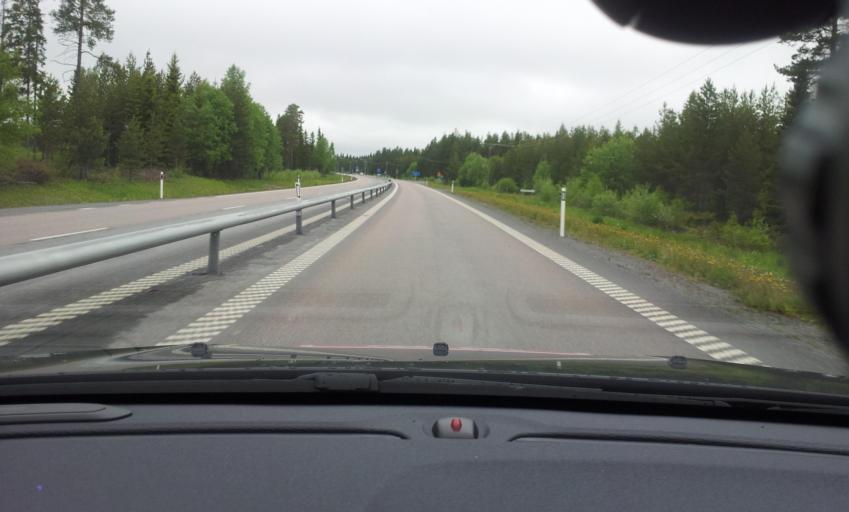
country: SE
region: Jaemtland
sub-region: OEstersunds Kommun
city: Ostersund
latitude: 63.2433
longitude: 14.5992
